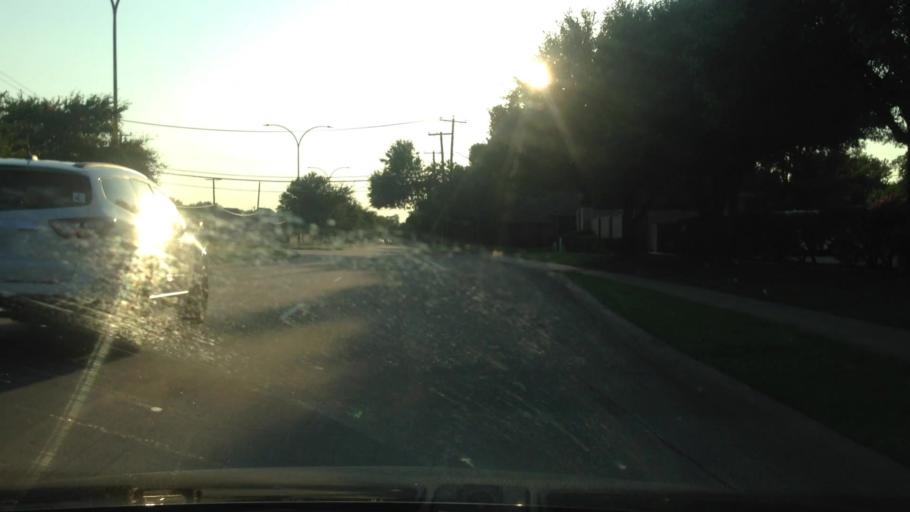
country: US
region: Texas
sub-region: Tarrant County
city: Dalworthington Gardens
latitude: 32.6487
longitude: -97.1372
